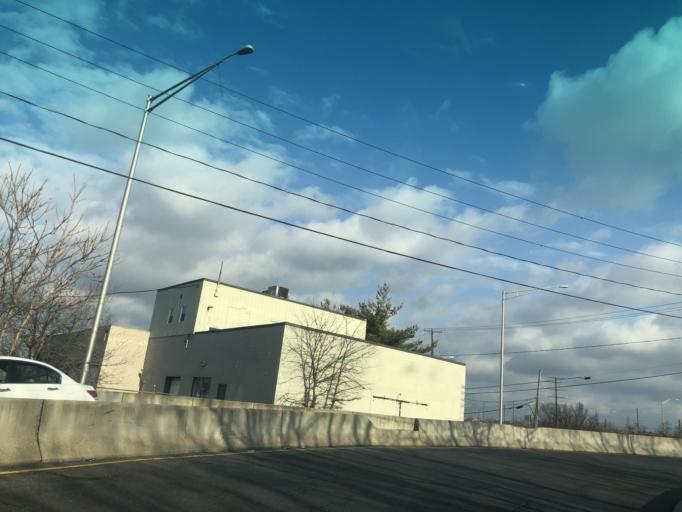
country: US
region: New Jersey
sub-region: Hudson County
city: Secaucus
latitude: 40.7661
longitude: -74.0702
